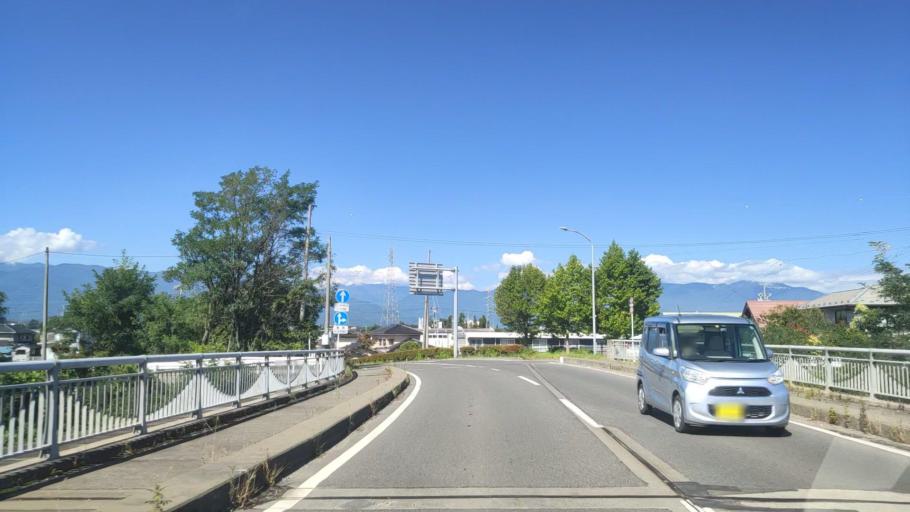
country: JP
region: Nagano
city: Shiojiri
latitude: 36.1645
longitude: 137.9439
